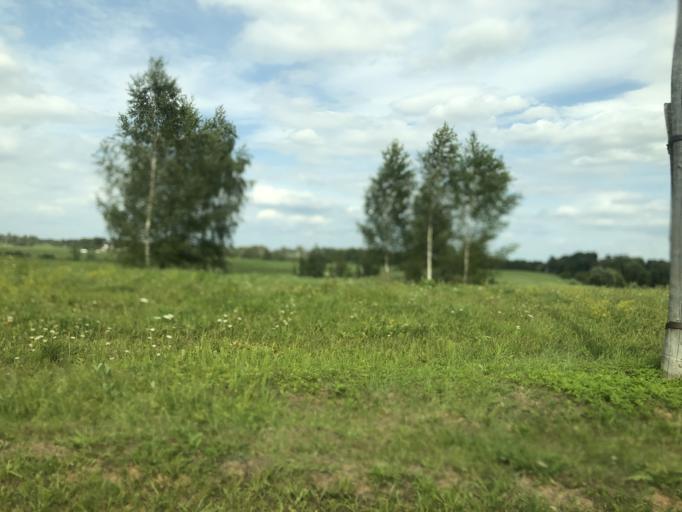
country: LV
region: Vecumnieki
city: Vecumnieki
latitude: 56.4601
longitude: 24.6004
